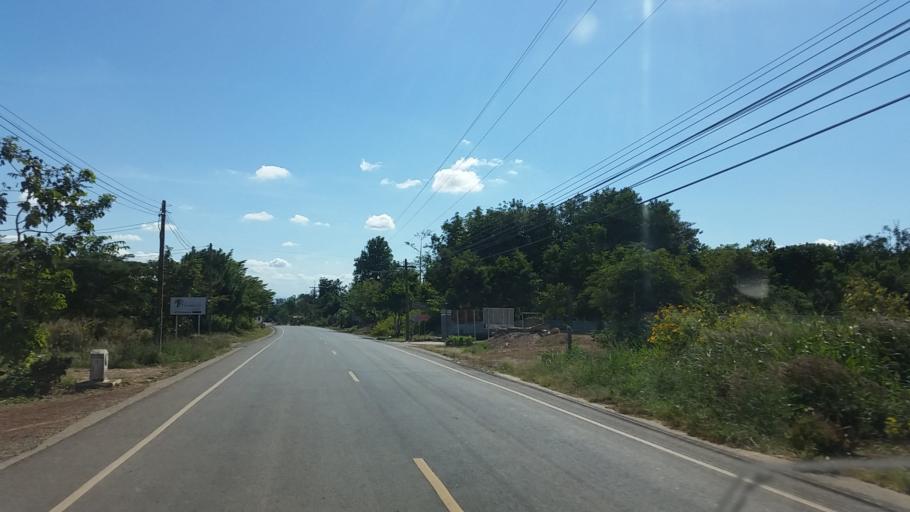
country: TH
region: Chaiyaphum
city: Thep Sathit
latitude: 15.5978
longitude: 101.4058
